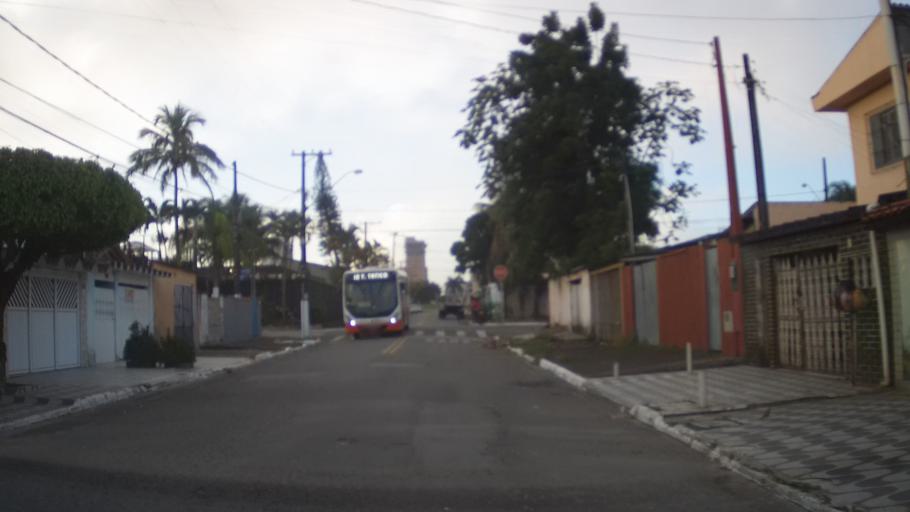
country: BR
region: Sao Paulo
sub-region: Praia Grande
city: Praia Grande
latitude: -24.0134
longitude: -46.4618
